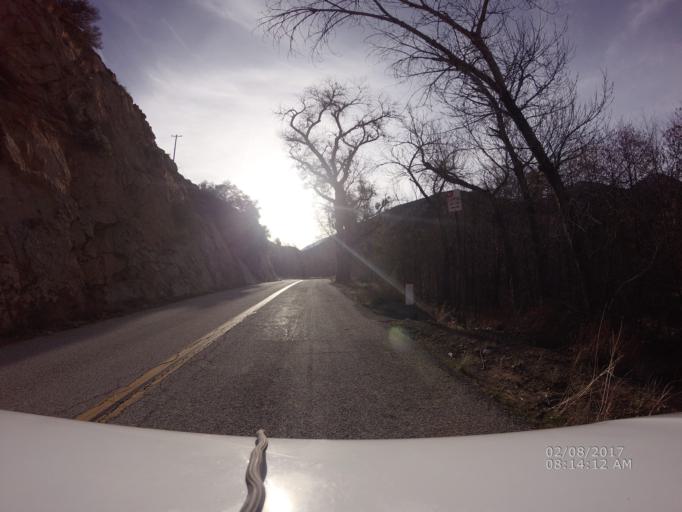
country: US
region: California
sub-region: Los Angeles County
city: Littlerock
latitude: 34.4164
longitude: -117.8362
